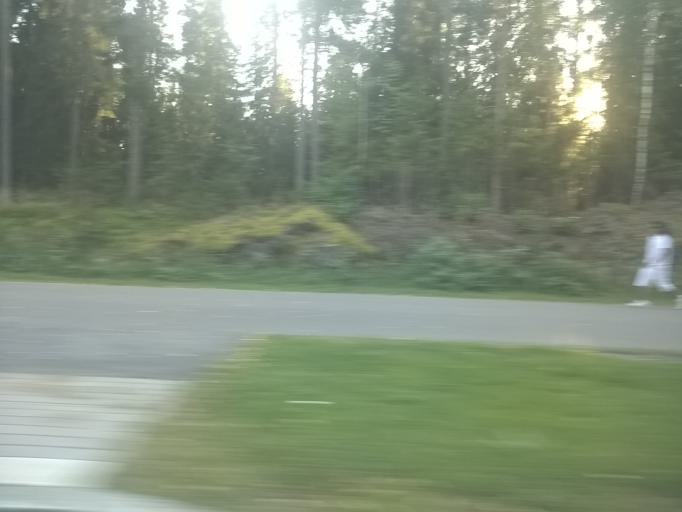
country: FI
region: Pirkanmaa
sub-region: Tampere
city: Tampere
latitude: 61.4409
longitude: 23.8443
